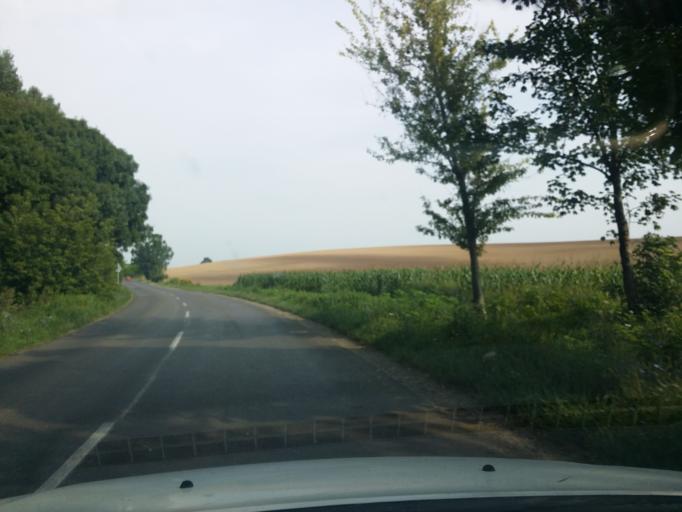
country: HU
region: Pest
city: Galgamacsa
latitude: 47.7284
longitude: 19.3772
